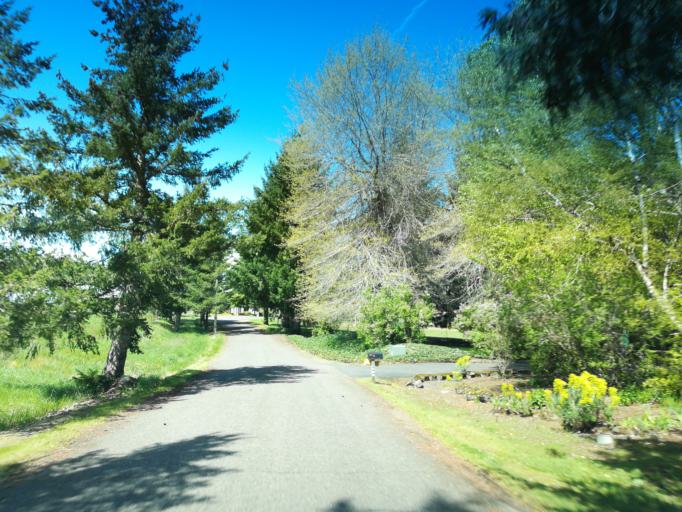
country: US
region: Oregon
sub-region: Clackamas County
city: Damascus
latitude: 45.4263
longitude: -122.4268
